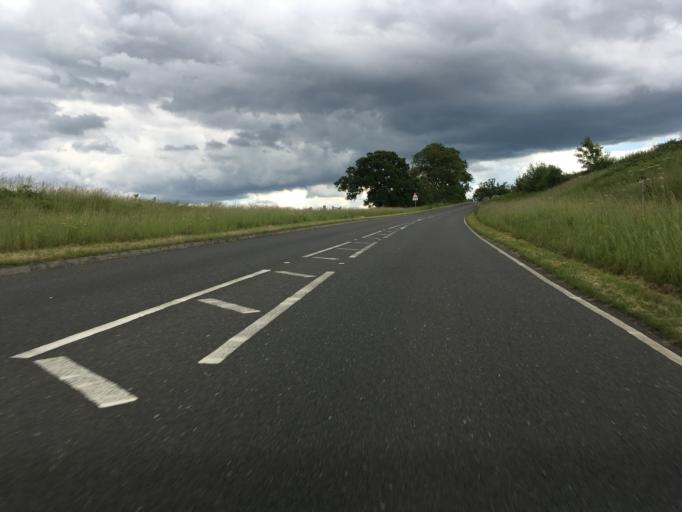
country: GB
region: England
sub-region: Central Bedfordshire
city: Leighton Buzzard
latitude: 51.9338
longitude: -0.6927
